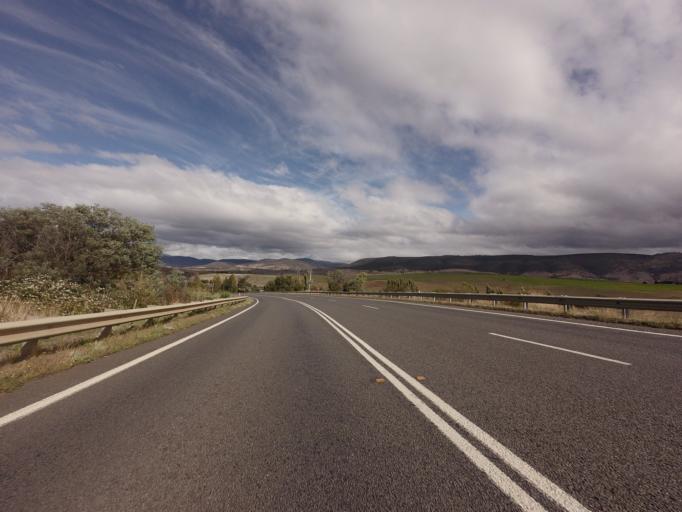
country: AU
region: Tasmania
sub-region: Derwent Valley
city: New Norfolk
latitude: -42.7203
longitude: 146.9483
